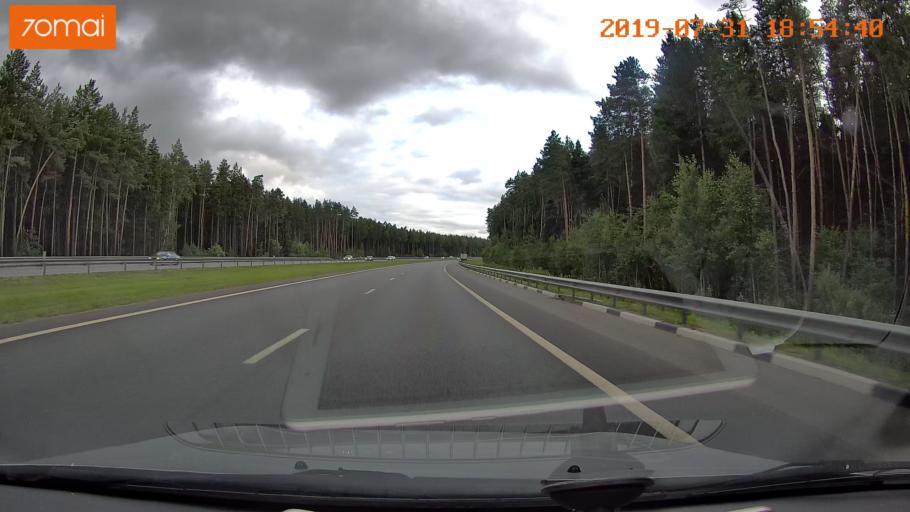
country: RU
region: Moskovskaya
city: Raduzhnyy
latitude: 55.1863
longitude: 38.6692
